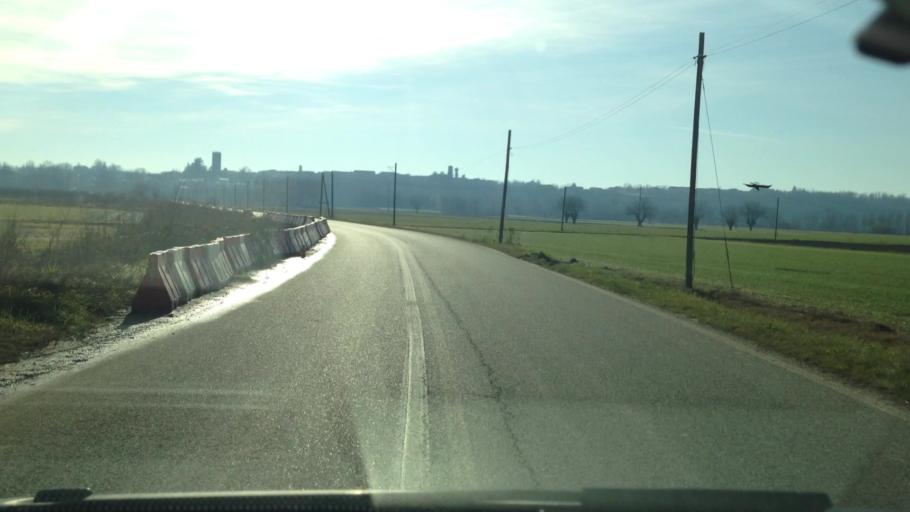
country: IT
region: Piedmont
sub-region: Provincia di Alessandria
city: Masio
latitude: 44.8810
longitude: 8.4092
